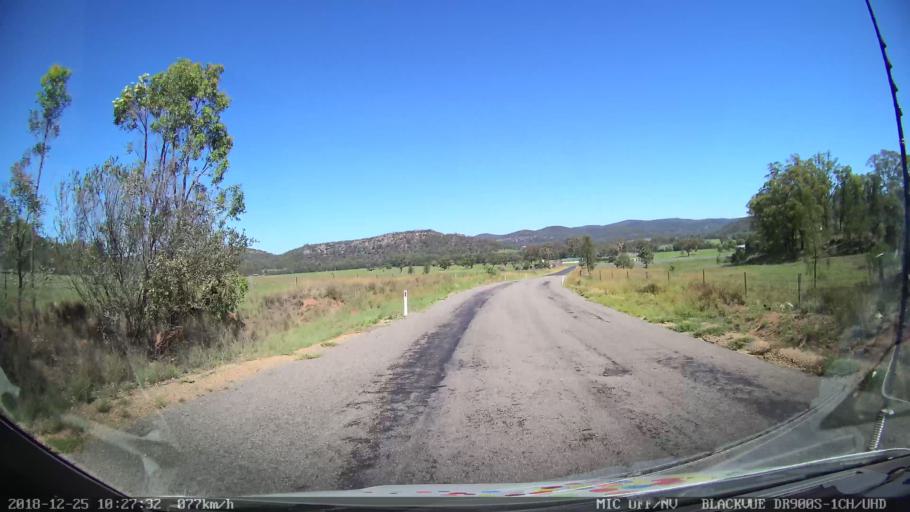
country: AU
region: New South Wales
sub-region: Muswellbrook
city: Denman
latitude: -32.3896
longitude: 150.4713
